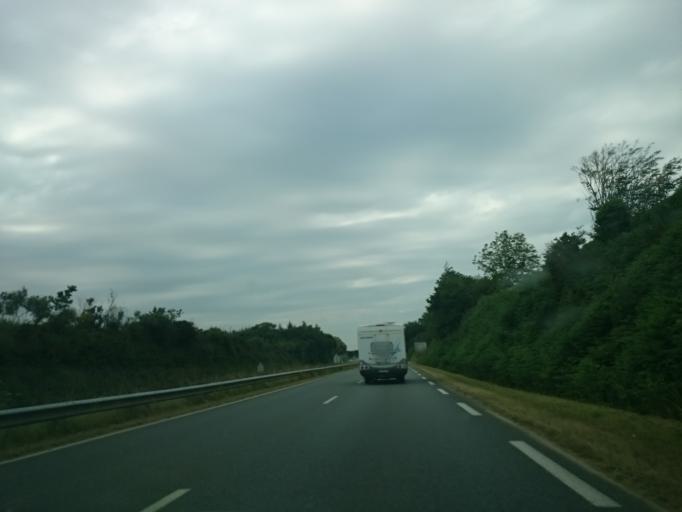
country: FR
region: Brittany
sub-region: Departement du Finistere
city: Guilers
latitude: 48.4211
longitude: -4.5646
